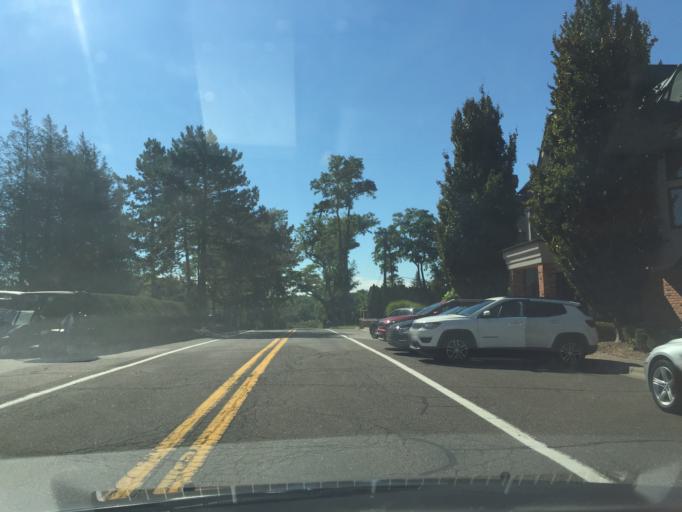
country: US
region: Michigan
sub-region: Oakland County
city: Sylvan Lake
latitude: 42.5972
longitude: -83.2970
